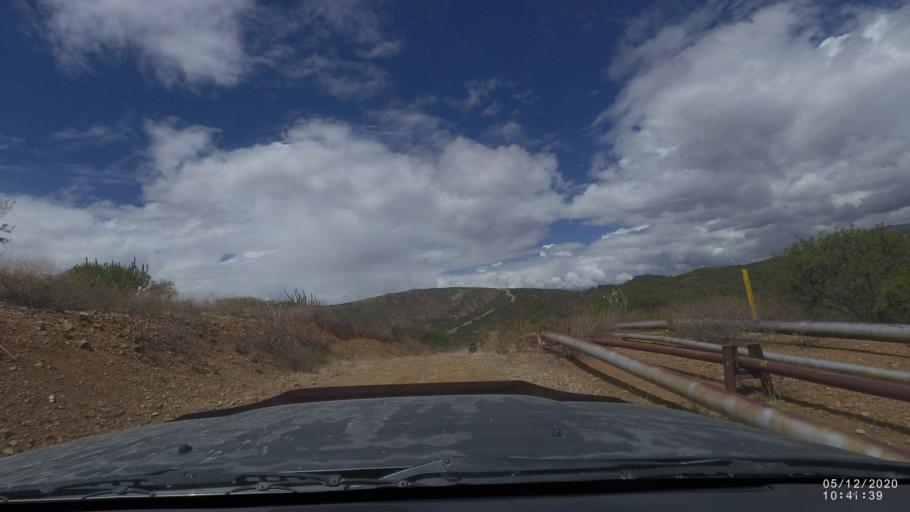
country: BO
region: Cochabamba
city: Sipe Sipe
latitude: -17.5466
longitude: -66.2927
